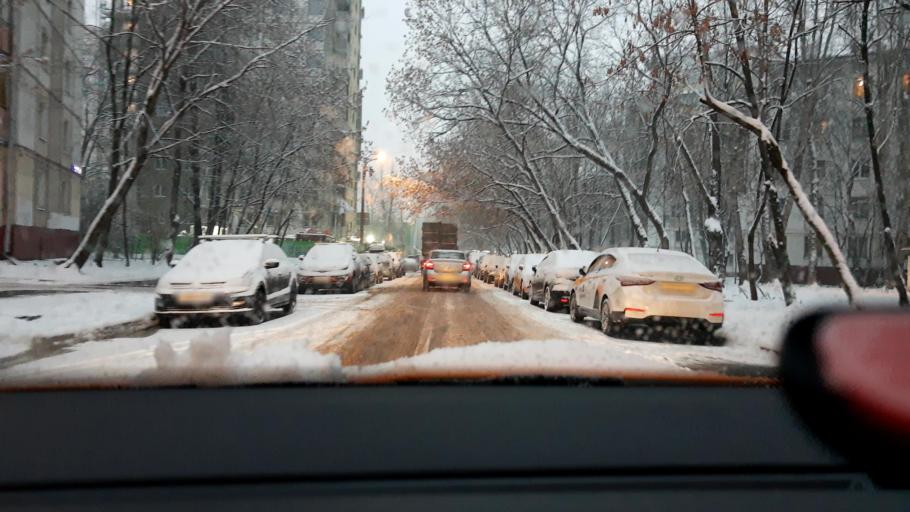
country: RU
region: Moscow
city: Novokuz'minki
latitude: 55.7091
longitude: 37.7724
